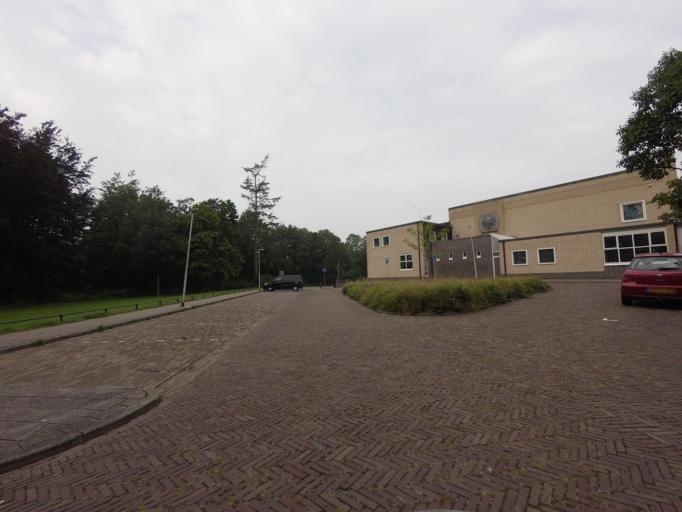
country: NL
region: Overijssel
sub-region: Gemeente Deventer
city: Deventer
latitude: 52.2598
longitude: 6.1562
